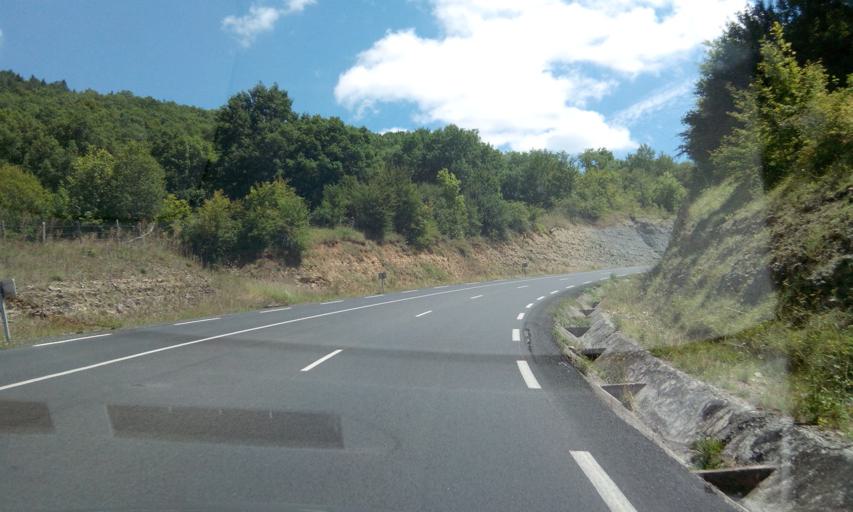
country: FR
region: Limousin
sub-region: Departement de la Correze
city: Meyssac
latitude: 45.0729
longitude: 1.6241
